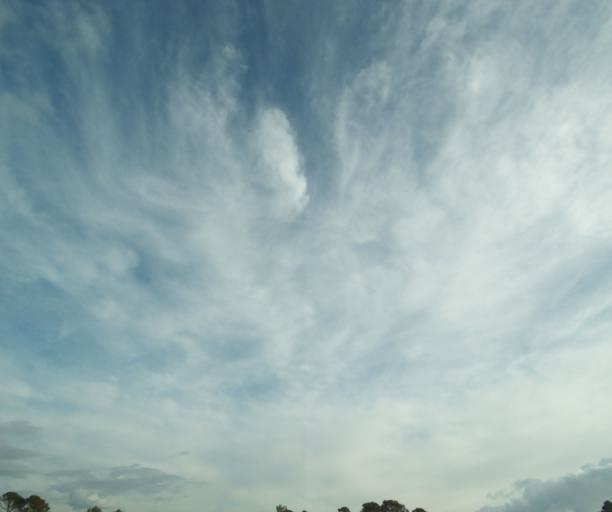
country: FR
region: Provence-Alpes-Cote d'Azur
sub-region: Departement du Var
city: Cabasse
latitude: 43.4070
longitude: 6.1863
